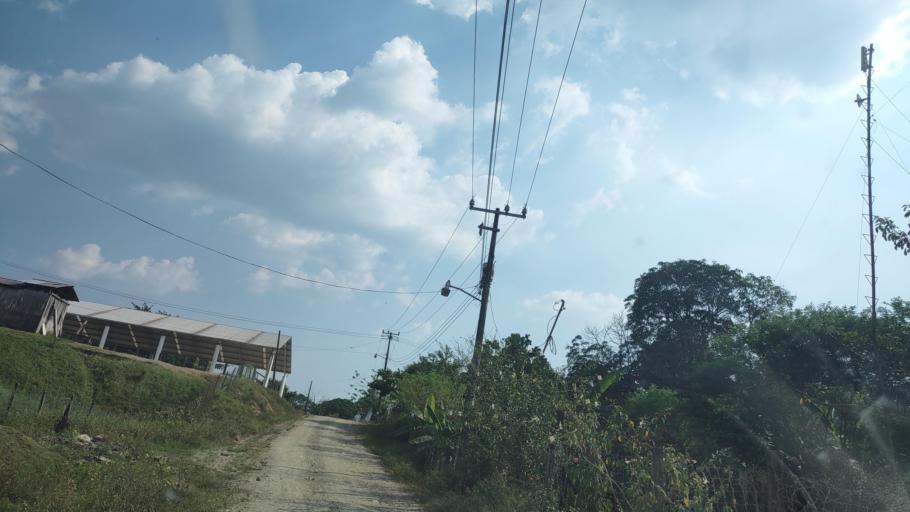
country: MX
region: Chiapas
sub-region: Tecpatan
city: Raudales Malpaso
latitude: 17.3247
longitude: -93.7458
